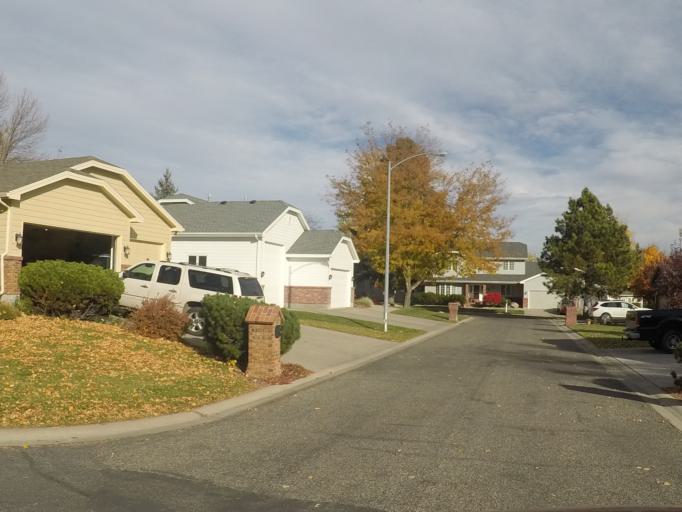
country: US
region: Montana
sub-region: Yellowstone County
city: Billings
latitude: 45.7964
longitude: -108.5607
